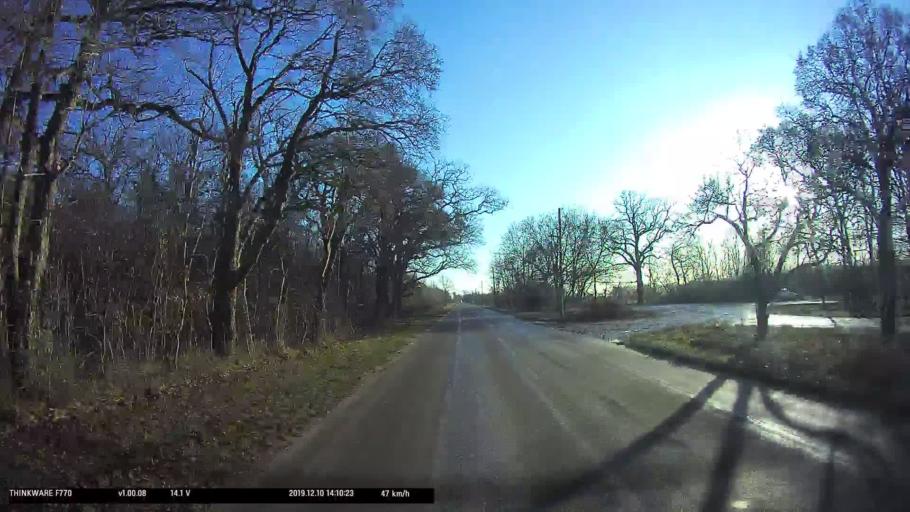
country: DK
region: Capital Region
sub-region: Tarnby Kommune
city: Tarnby
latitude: 55.5726
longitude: 12.5809
